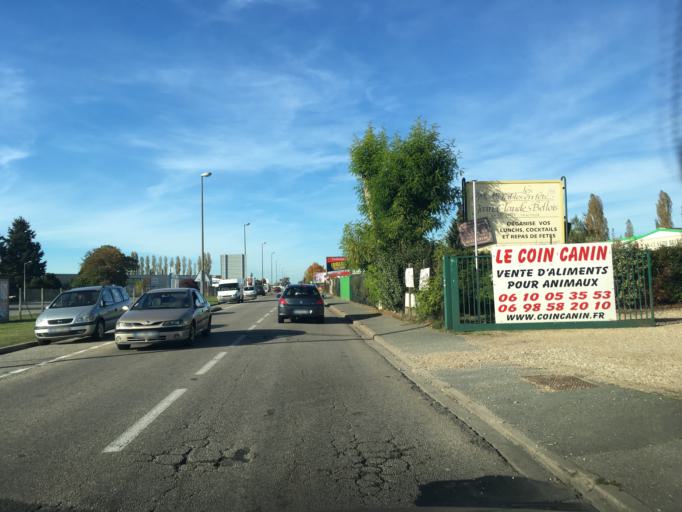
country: FR
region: Haute-Normandie
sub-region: Departement de l'Eure
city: Evreux
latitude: 49.0160
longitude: 1.1870
